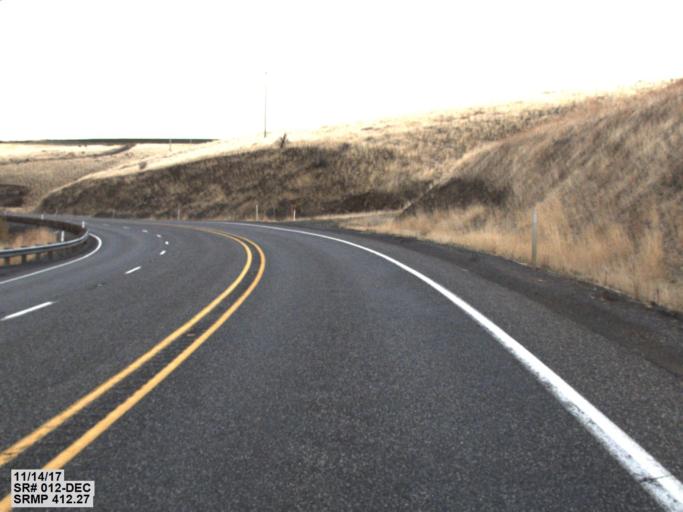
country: US
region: Washington
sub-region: Garfield County
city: Pomeroy
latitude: 46.4437
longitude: -117.4406
